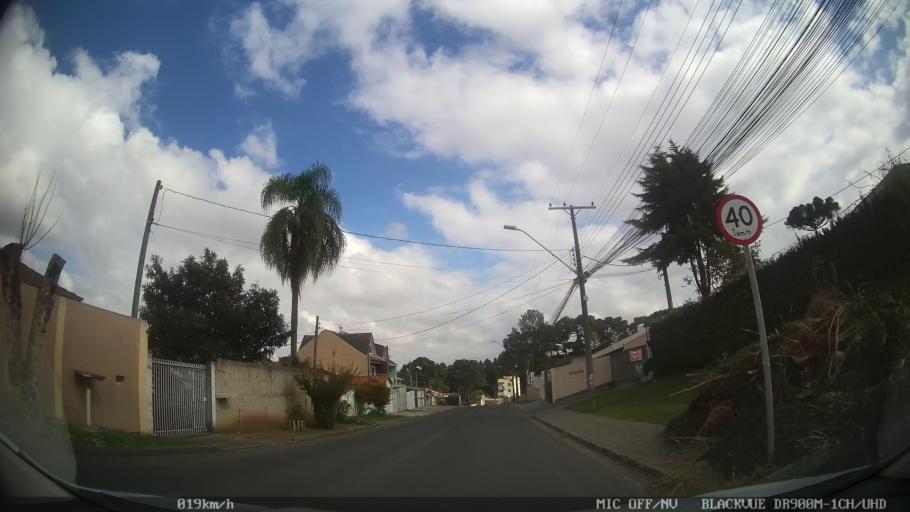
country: BR
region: Parana
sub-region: Colombo
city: Colombo
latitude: -25.3564
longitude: -49.2092
